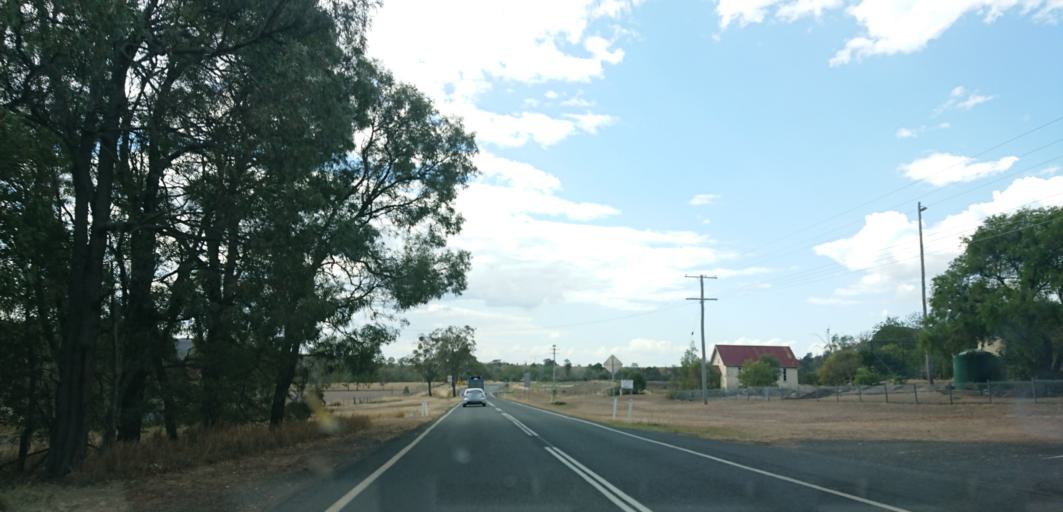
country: AU
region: Queensland
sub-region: Lockyer Valley
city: Gatton
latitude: -27.6651
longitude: 152.1599
